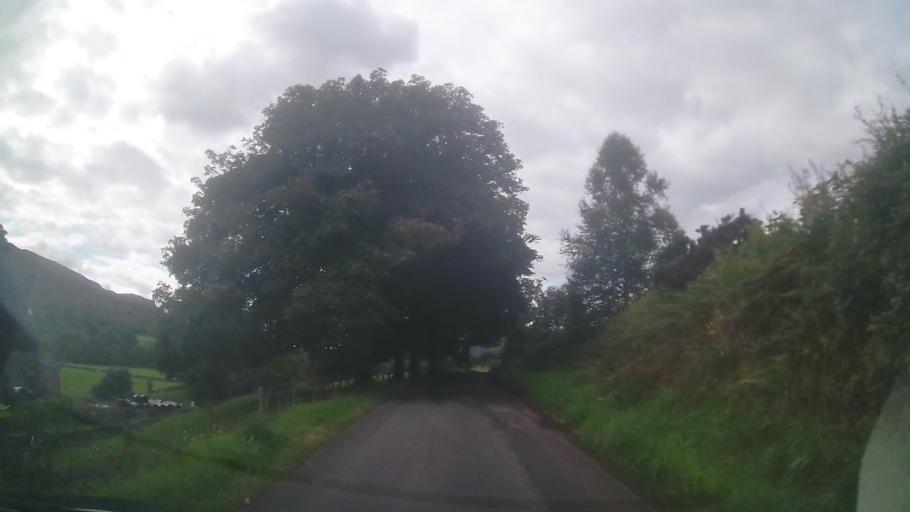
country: GB
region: England
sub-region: Cumbria
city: Millom
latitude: 54.3973
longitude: -3.2324
